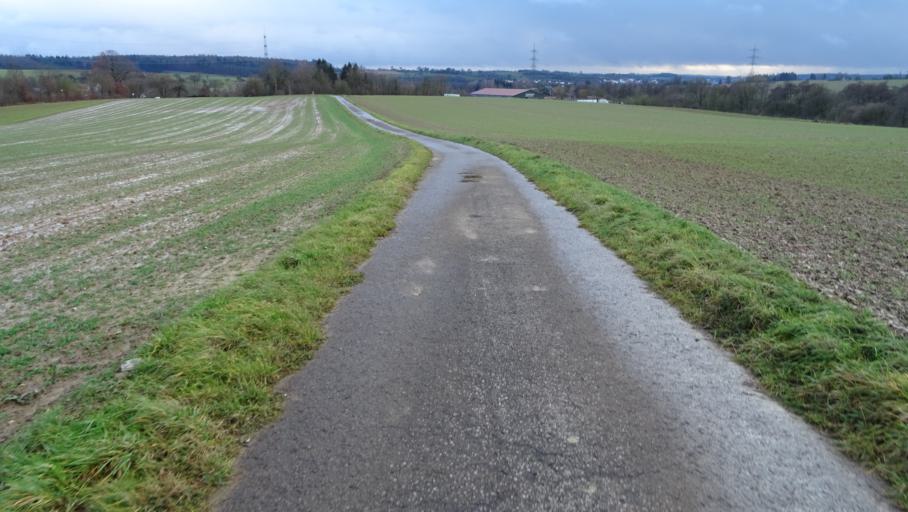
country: DE
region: Baden-Wuerttemberg
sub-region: Karlsruhe Region
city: Seckach
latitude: 49.4338
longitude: 9.2869
